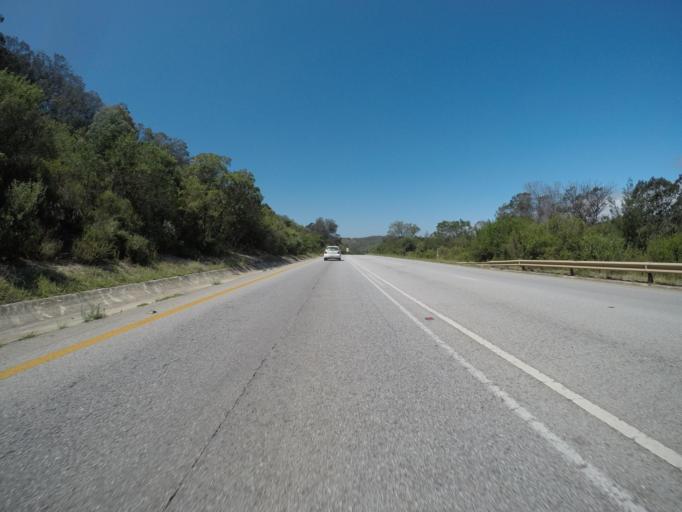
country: ZA
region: Eastern Cape
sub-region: Cacadu District Municipality
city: Jeffrey's Bay
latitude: -33.9039
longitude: 25.0802
